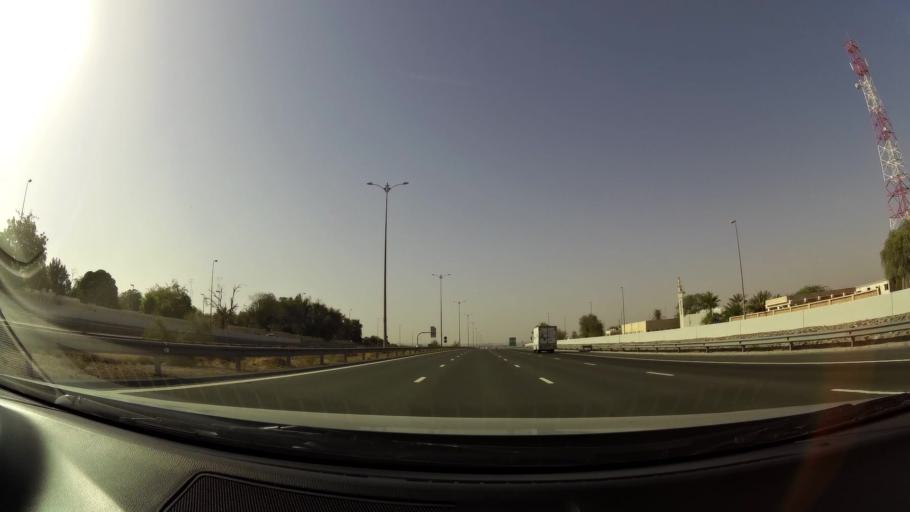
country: OM
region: Al Buraimi
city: Al Buraymi
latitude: 24.5778
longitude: 55.7446
